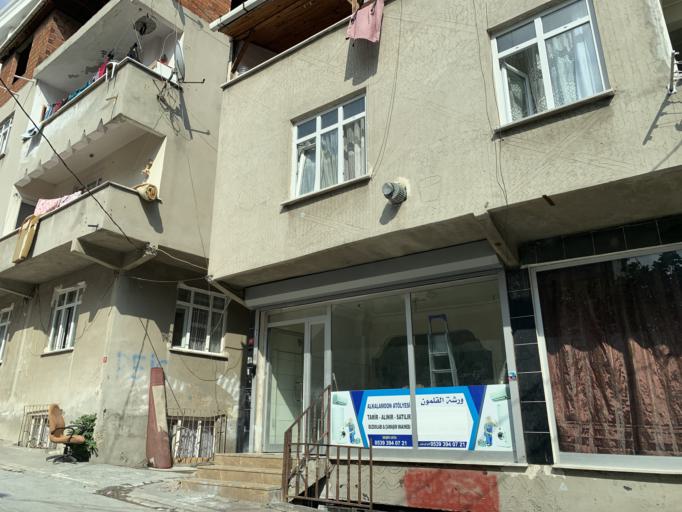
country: TR
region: Istanbul
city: Esenyurt
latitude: 41.0339
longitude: 28.6727
